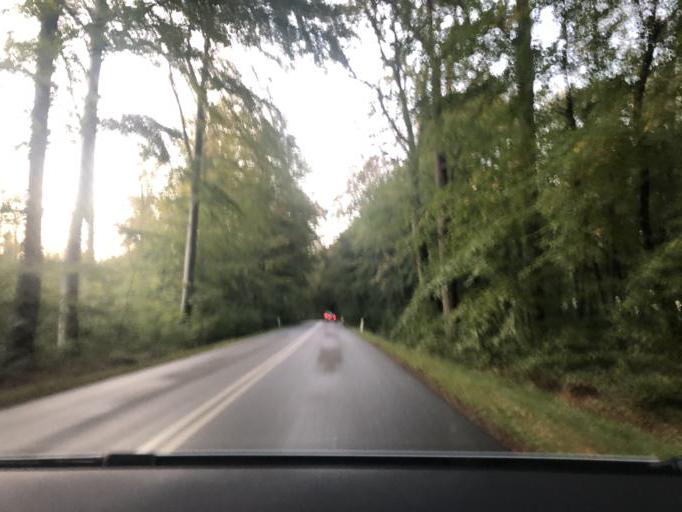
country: DK
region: Capital Region
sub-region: Frederikssund Kommune
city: Slangerup
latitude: 55.8181
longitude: 12.2013
